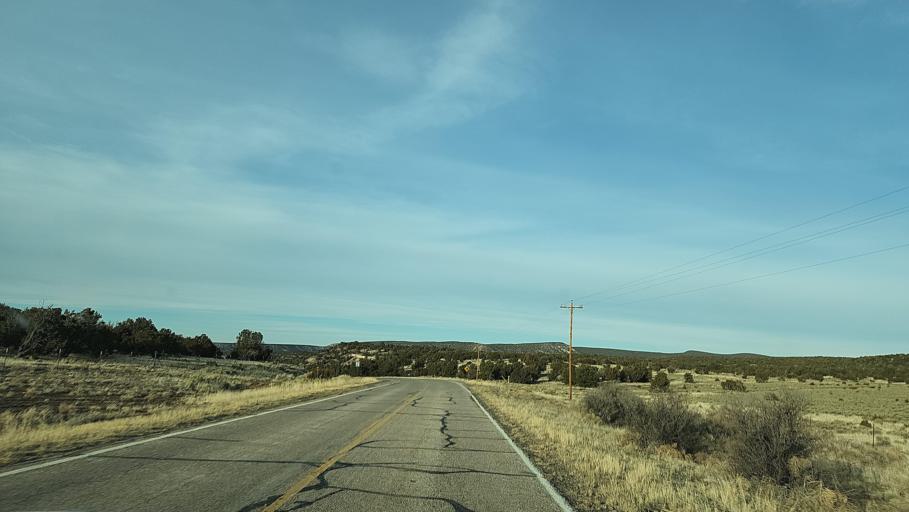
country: US
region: New Mexico
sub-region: McKinley County
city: Black Rock
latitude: 34.4147
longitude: -108.4316
